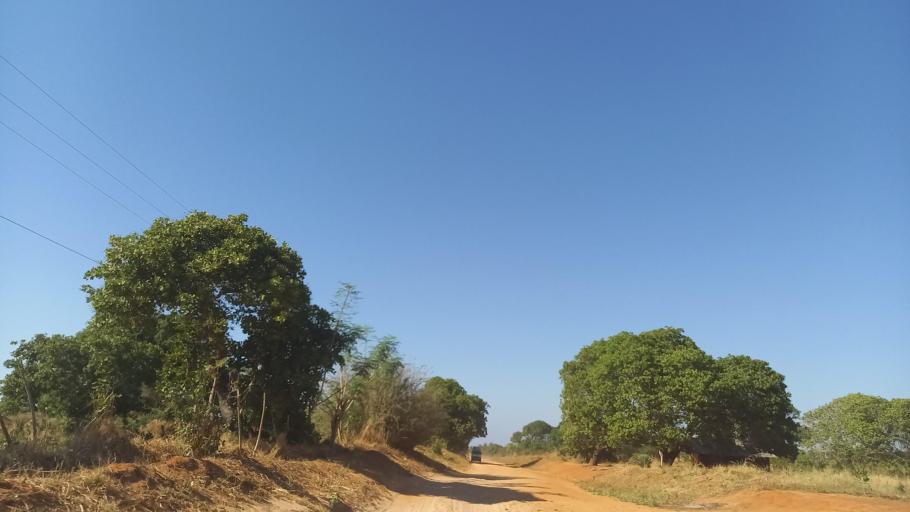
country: MZ
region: Cabo Delgado
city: Pemba
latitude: -13.1518
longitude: 40.5575
